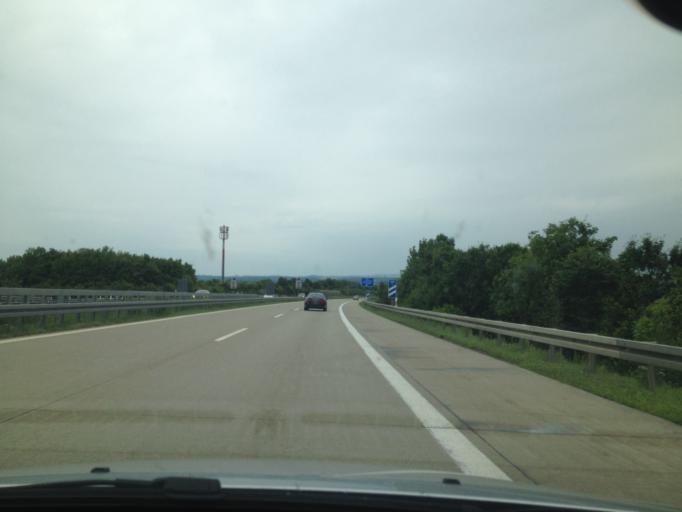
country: DE
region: Baden-Wuerttemberg
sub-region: Regierungsbezirk Stuttgart
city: Westhausen
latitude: 48.8815
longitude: 10.1649
